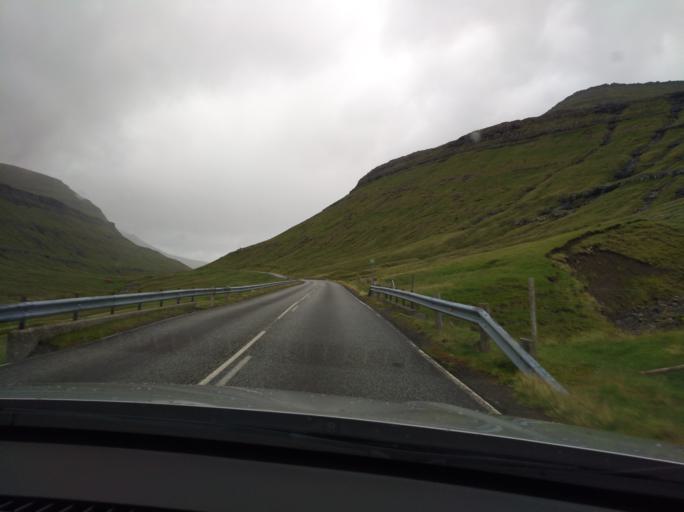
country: FO
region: Eysturoy
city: Fuglafjordur
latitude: 62.2253
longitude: -6.8799
